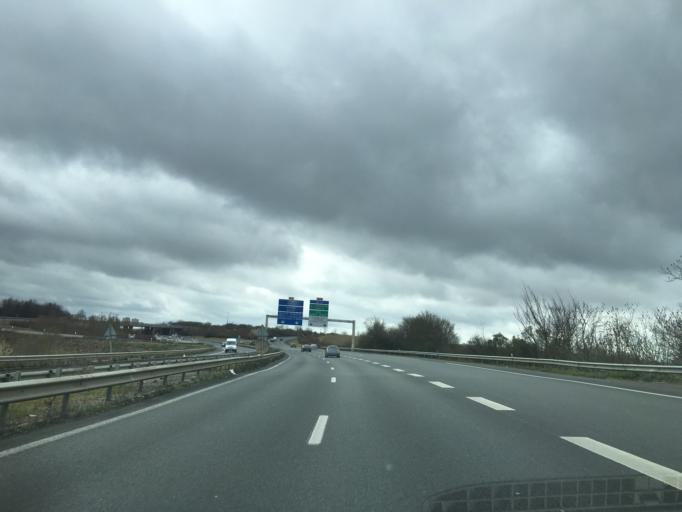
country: FR
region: Ile-de-France
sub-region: Departement de Seine-et-Marne
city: Brie-Comte-Robert
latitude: 48.6579
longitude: 2.6128
